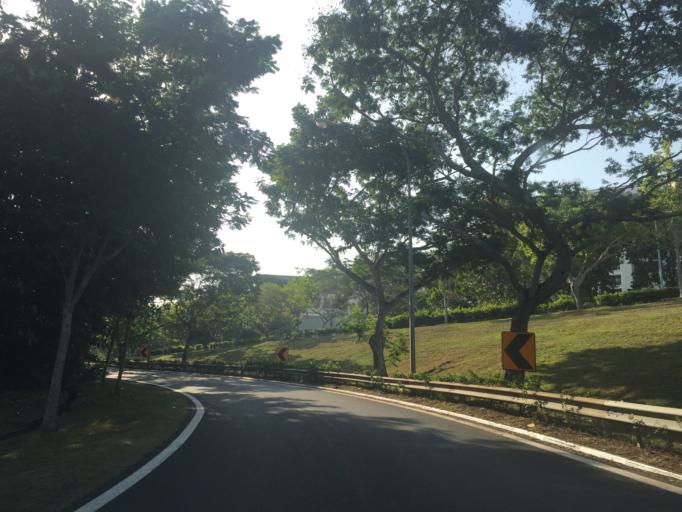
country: SG
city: Singapore
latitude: 1.3430
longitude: 103.9475
